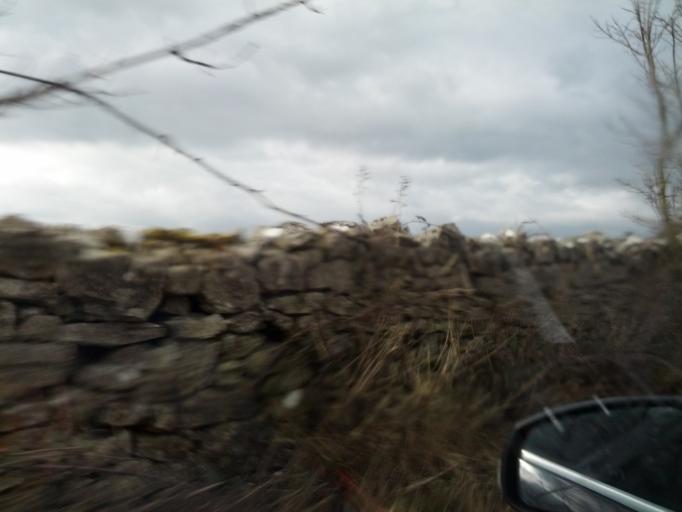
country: IE
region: Connaught
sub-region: County Galway
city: Athenry
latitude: 53.4451
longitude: -8.6351
